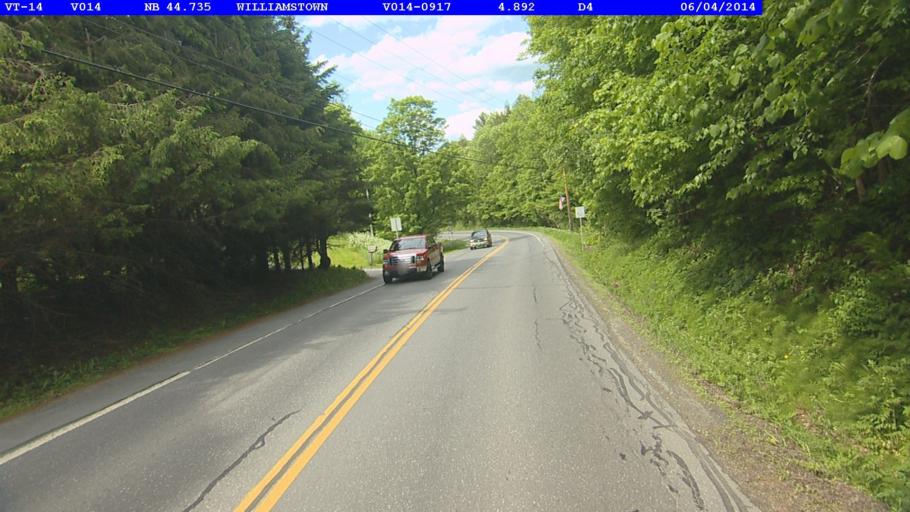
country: US
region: Vermont
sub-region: Orange County
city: Williamstown
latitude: 44.1270
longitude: -72.5373
